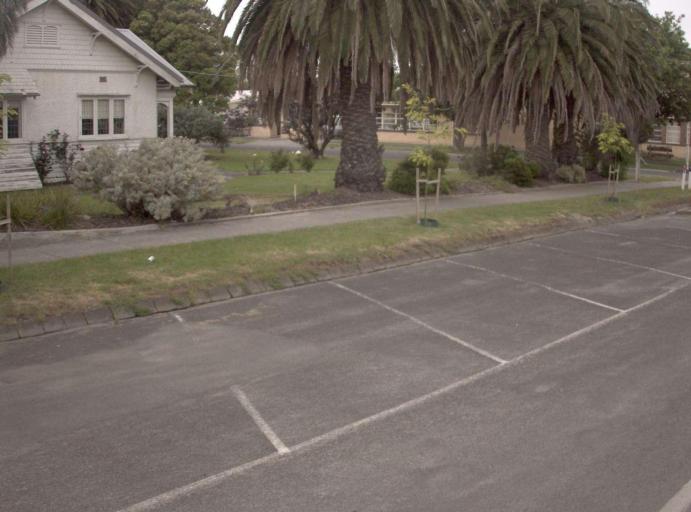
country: AU
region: Victoria
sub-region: Latrobe
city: Traralgon
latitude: -38.5606
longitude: 146.6767
